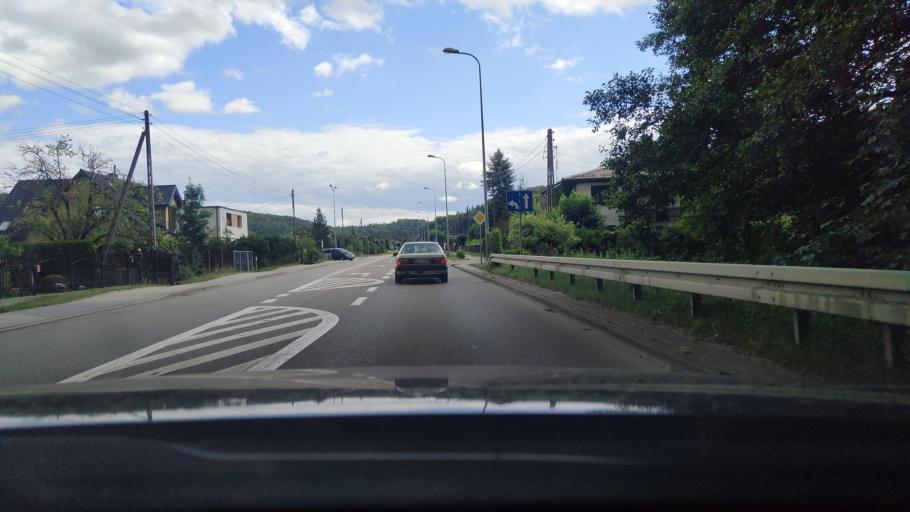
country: PL
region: Pomeranian Voivodeship
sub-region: Powiat wejherowski
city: Wejherowo
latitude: 54.5908
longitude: 18.2414
